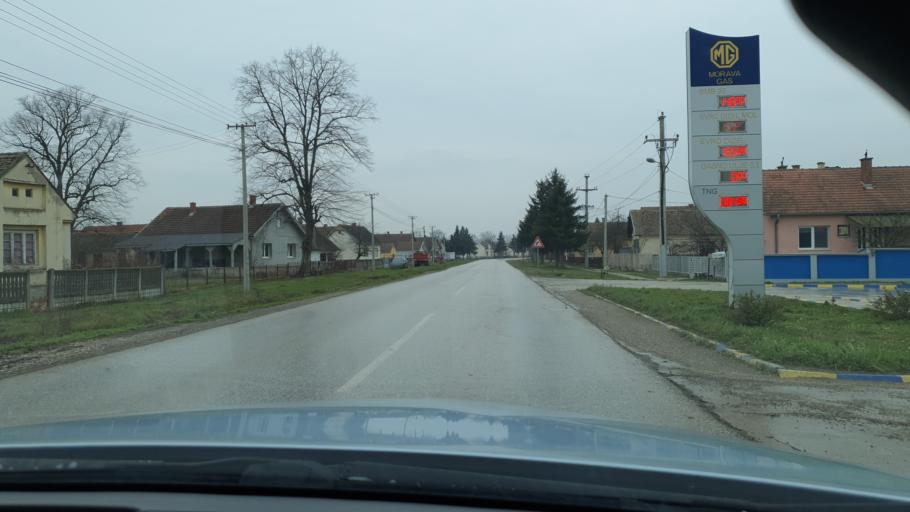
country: RS
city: Stitar
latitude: 44.7850
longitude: 19.5958
